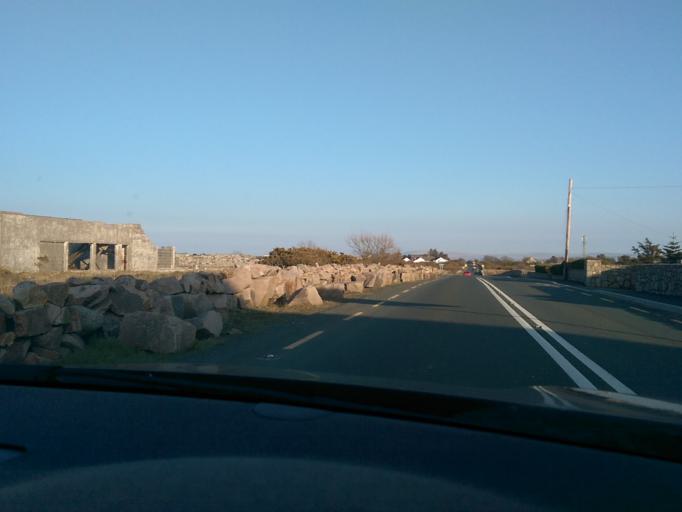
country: IE
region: Connaught
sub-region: County Galway
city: Oughterard
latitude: 53.2412
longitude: -9.5020
